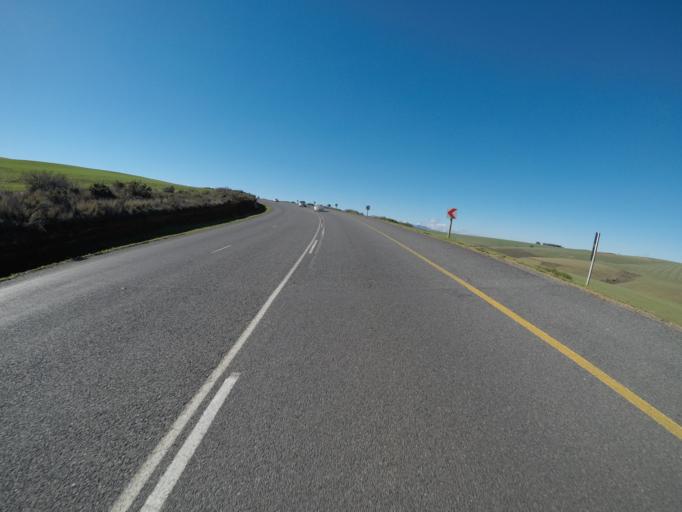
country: ZA
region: Western Cape
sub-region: Overberg District Municipality
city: Caledon
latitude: -34.2291
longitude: 19.2708
